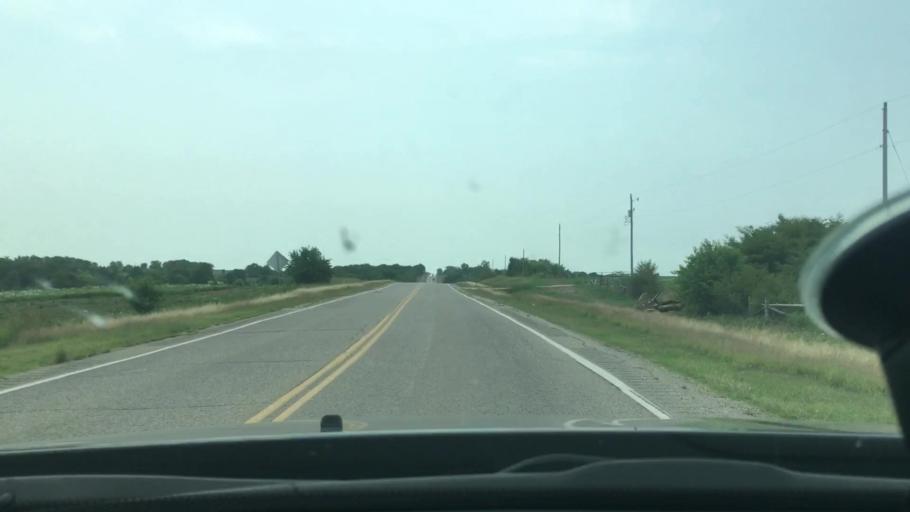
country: US
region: Oklahoma
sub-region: Marshall County
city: Madill
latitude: 34.0622
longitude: -96.7611
